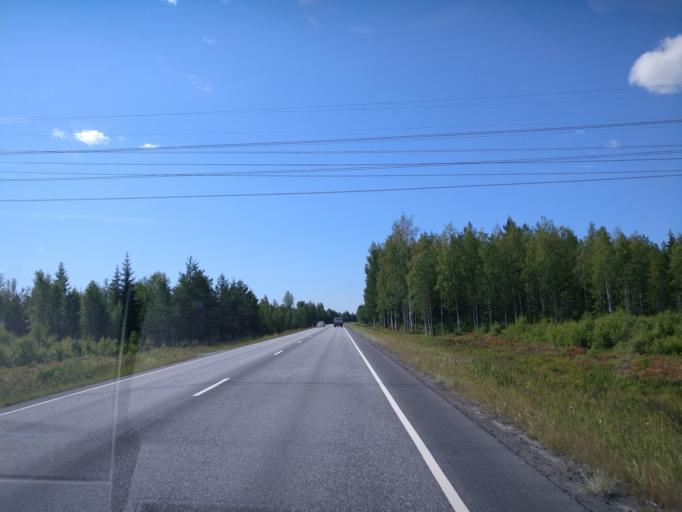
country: FI
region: Satakunta
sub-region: Pori
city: Kullaa
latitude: 61.4582
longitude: 22.0717
